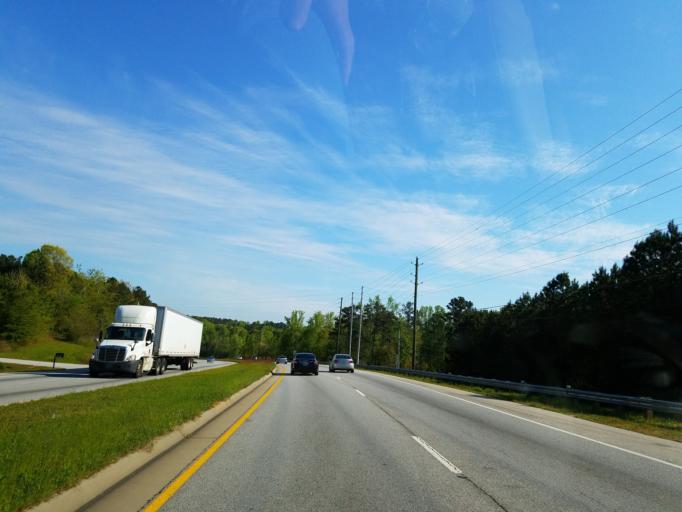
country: US
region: Georgia
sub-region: Douglas County
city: Lithia Springs
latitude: 33.7104
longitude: -84.6630
